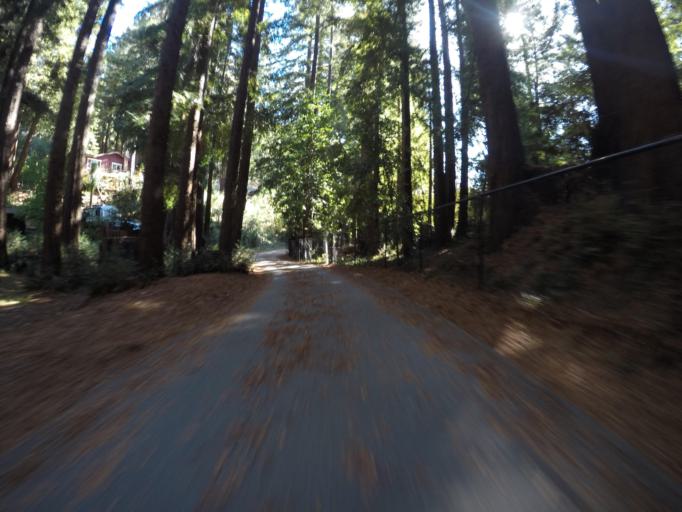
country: US
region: California
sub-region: Santa Cruz County
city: Scotts Valley
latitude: 37.0579
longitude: -122.0197
